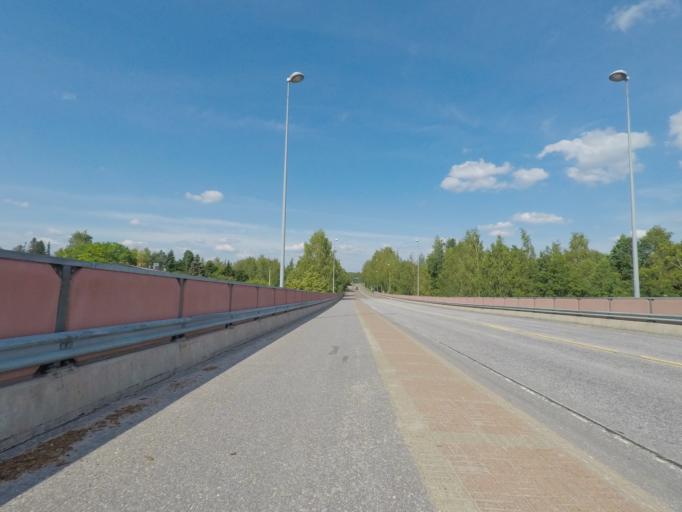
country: FI
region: Southern Savonia
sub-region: Mikkeli
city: Puumala
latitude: 61.5214
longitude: 28.1796
